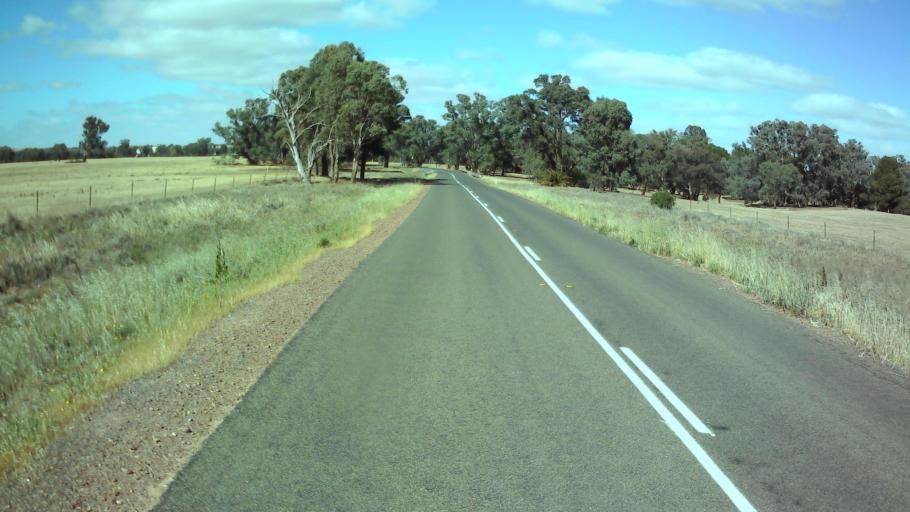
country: AU
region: New South Wales
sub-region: Weddin
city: Grenfell
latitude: -33.9879
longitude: 148.4112
